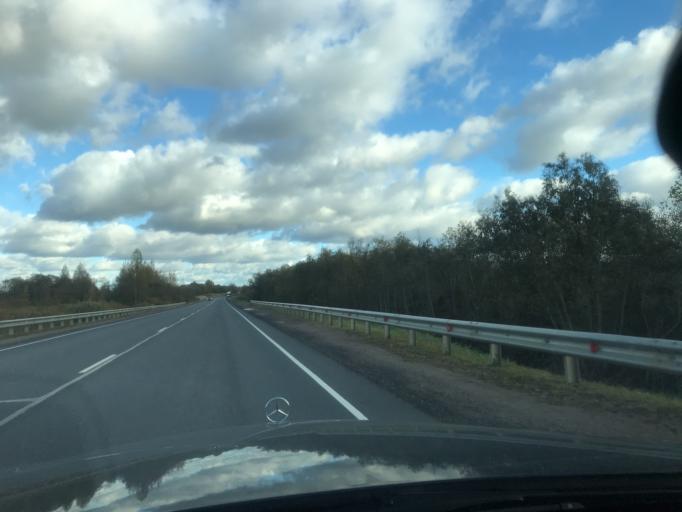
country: RU
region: Pskov
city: Novosokol'niki
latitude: 56.3299
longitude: 30.0841
